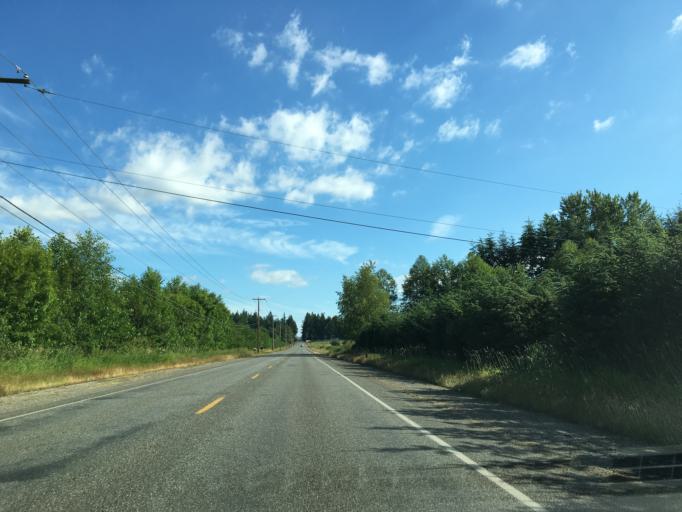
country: US
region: Washington
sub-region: Whatcom County
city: Ferndale
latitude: 48.9193
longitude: -122.5747
